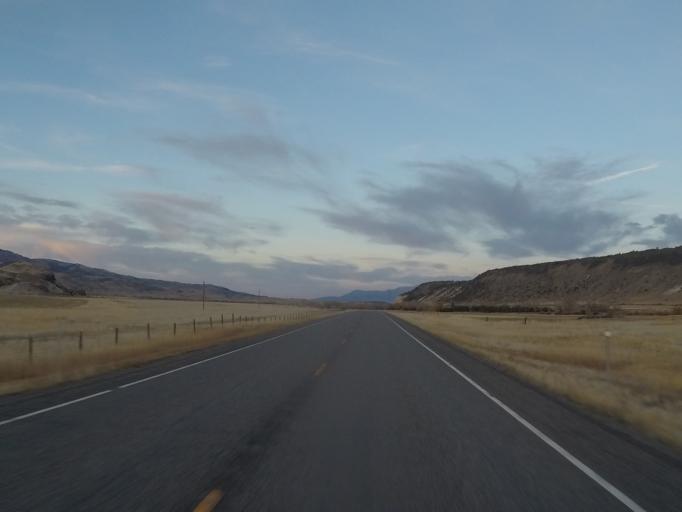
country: US
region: Montana
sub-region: Gallatin County
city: Bozeman
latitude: 45.2810
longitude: -110.8504
